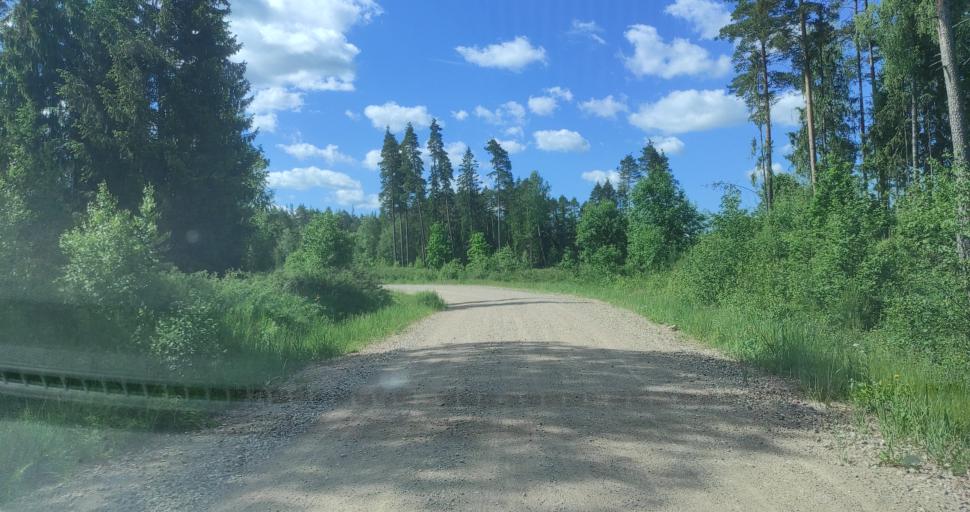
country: LV
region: Kuldigas Rajons
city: Kuldiga
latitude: 56.9451
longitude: 21.7888
